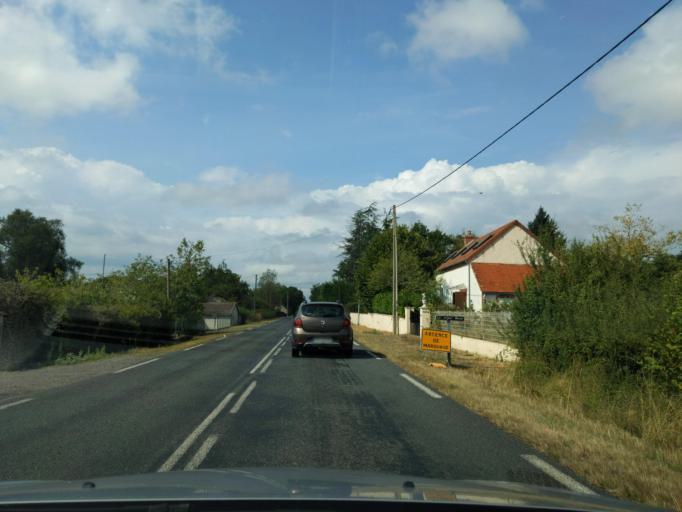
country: FR
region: Bourgogne
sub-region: Departement de Saone-et-Loire
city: Bourbon-Lancy
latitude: 46.6763
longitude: 3.8106
